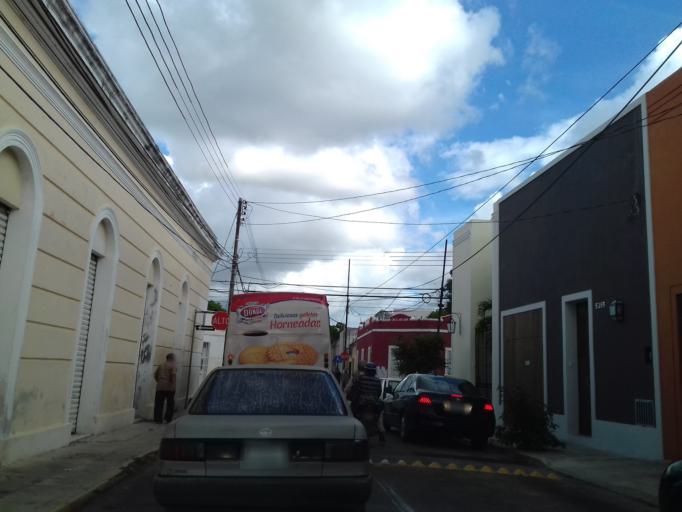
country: MX
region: Yucatan
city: Merida
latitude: 20.9721
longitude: -89.6278
